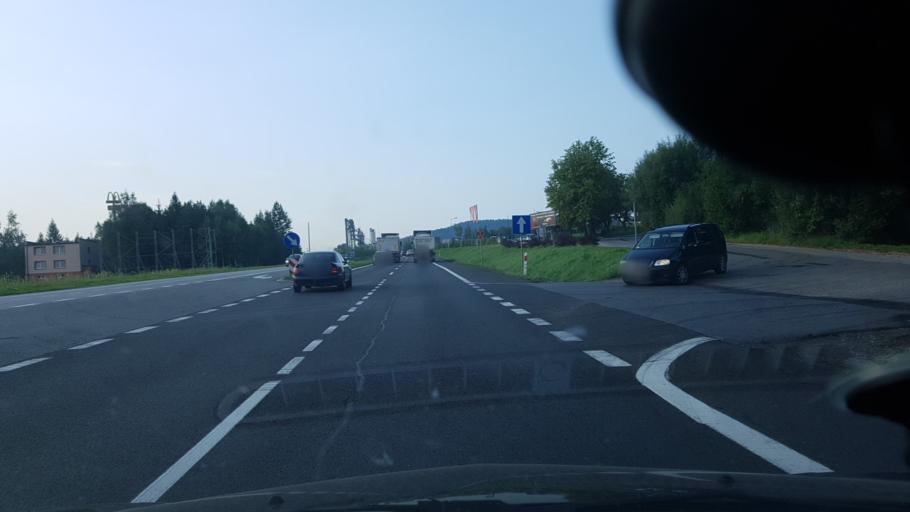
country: PL
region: Lesser Poland Voivodeship
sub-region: Powiat myslenicki
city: Jawornik
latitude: 49.8688
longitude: 19.9086
